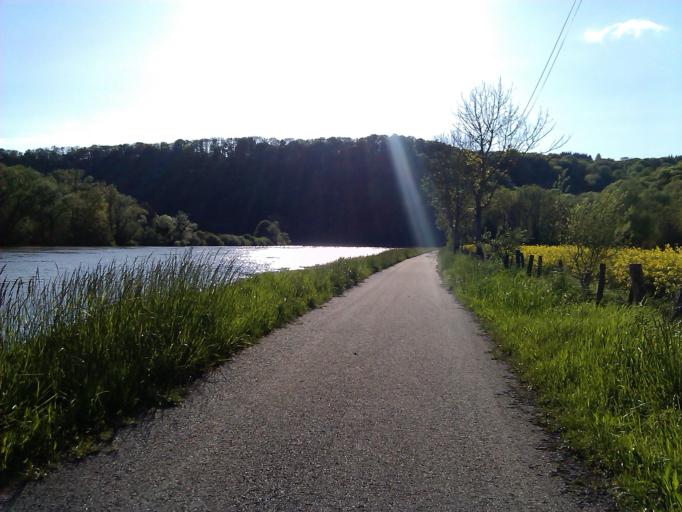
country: FR
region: Franche-Comte
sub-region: Departement du Doubs
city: Clerval
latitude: 47.4412
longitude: 6.5397
